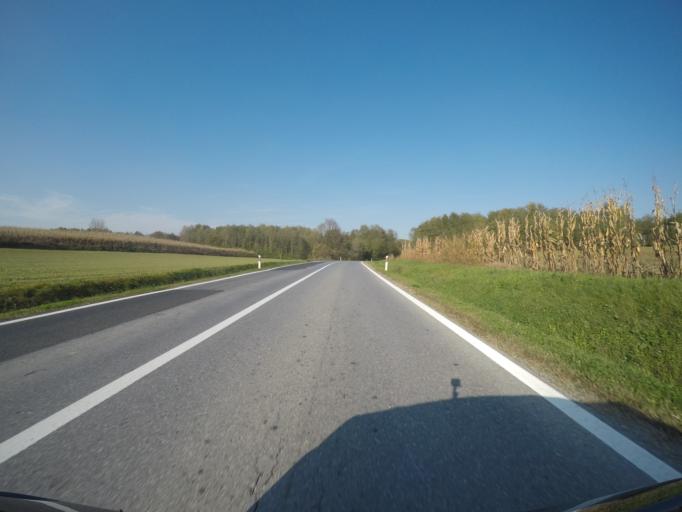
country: HR
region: Koprivnicko-Krizevacka
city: Virje
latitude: 46.0211
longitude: 16.9734
